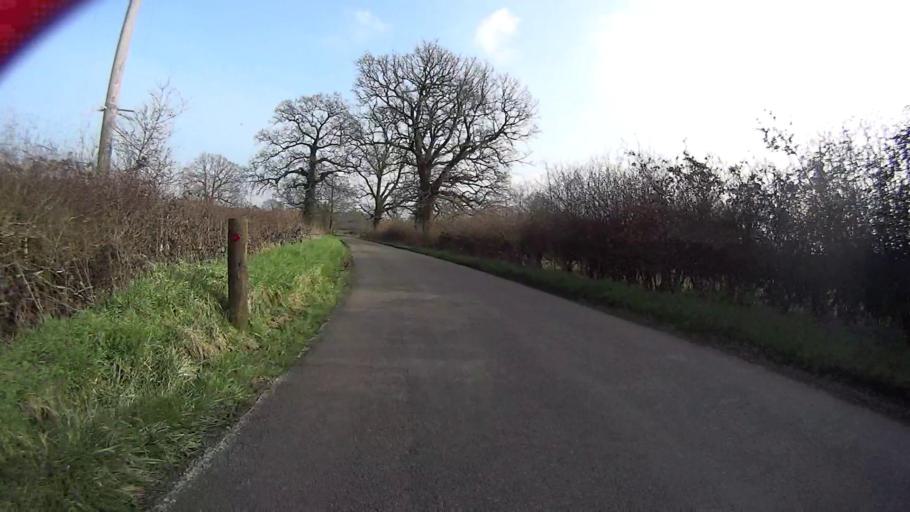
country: GB
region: England
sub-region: Surrey
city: Felbridge
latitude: 51.1657
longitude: -0.0670
